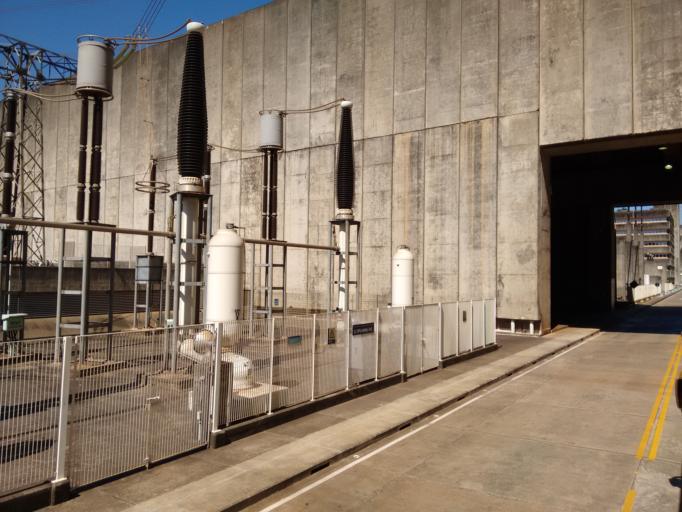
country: PY
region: Alto Parana
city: Ciudad del Este
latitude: -25.4085
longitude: -54.5864
